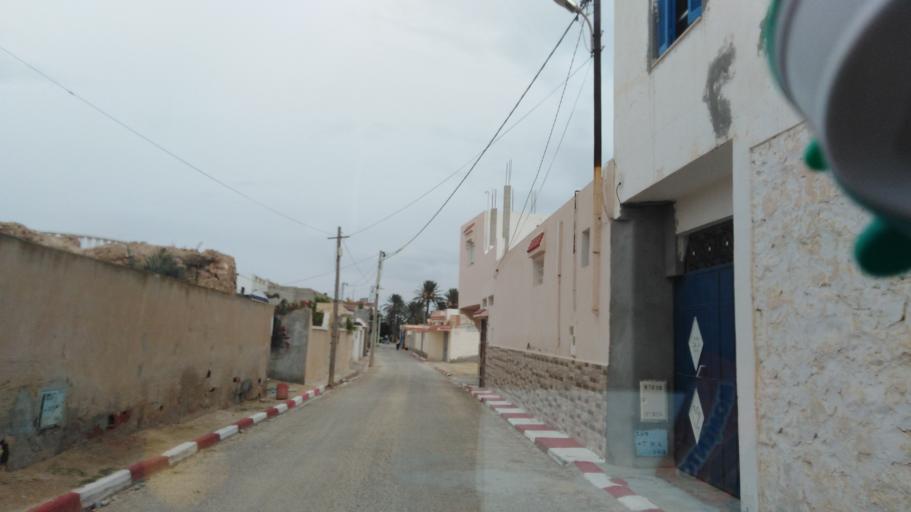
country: TN
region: Qabis
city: Gabes
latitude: 33.9574
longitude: 10.0028
